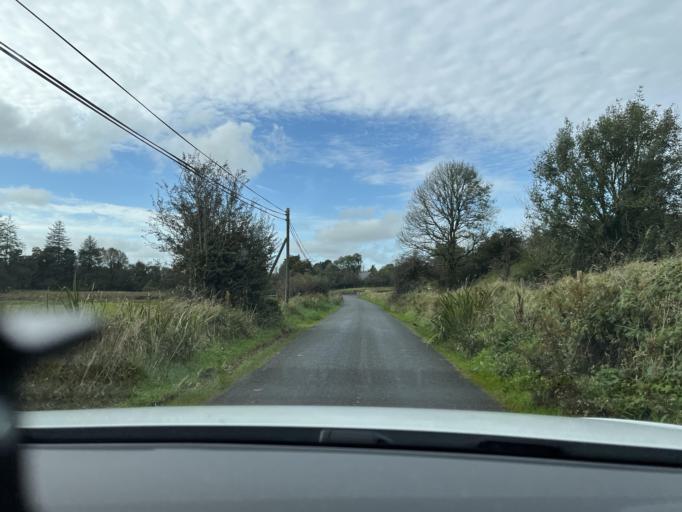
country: IE
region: Connaught
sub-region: Roscommon
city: Boyle
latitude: 54.0231
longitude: -8.3908
